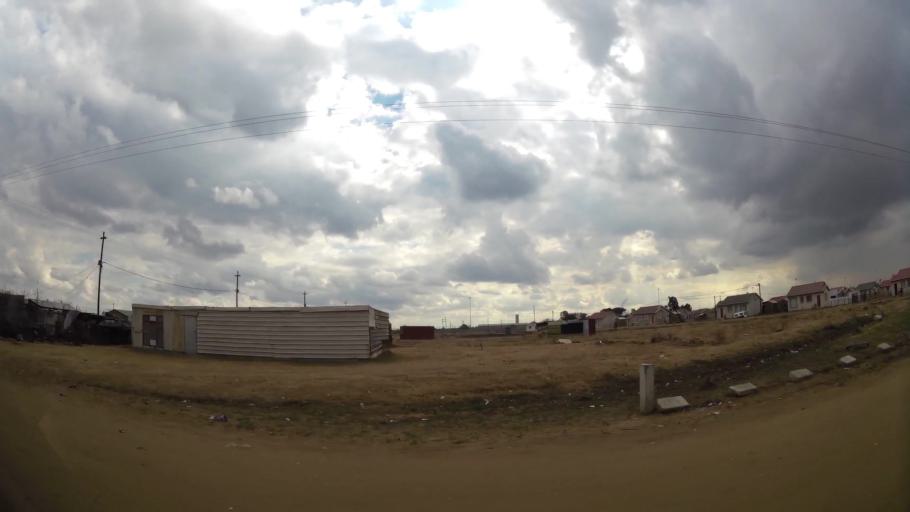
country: ZA
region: Orange Free State
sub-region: Fezile Dabi District Municipality
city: Sasolburg
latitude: -26.8595
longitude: 27.8666
